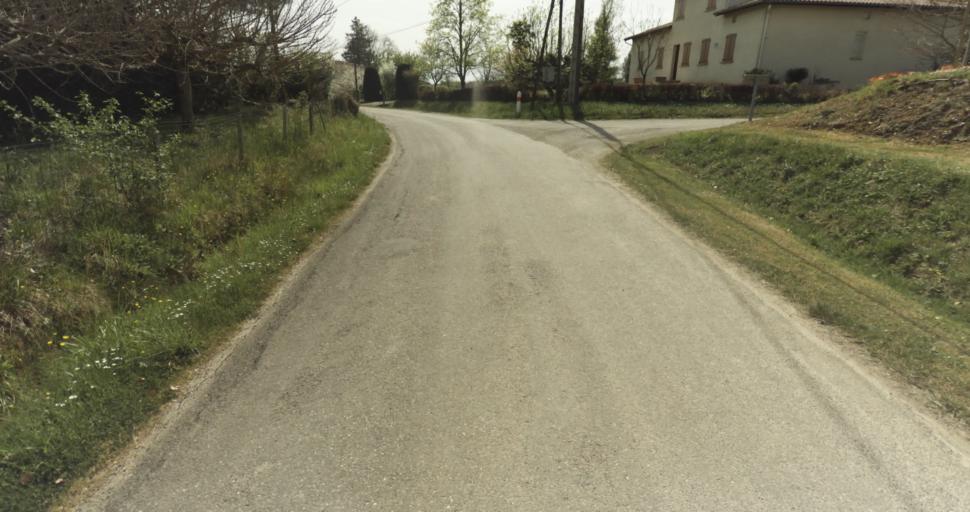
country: FR
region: Midi-Pyrenees
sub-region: Departement du Tarn-et-Garonne
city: Moissac
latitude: 44.1354
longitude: 1.0934
